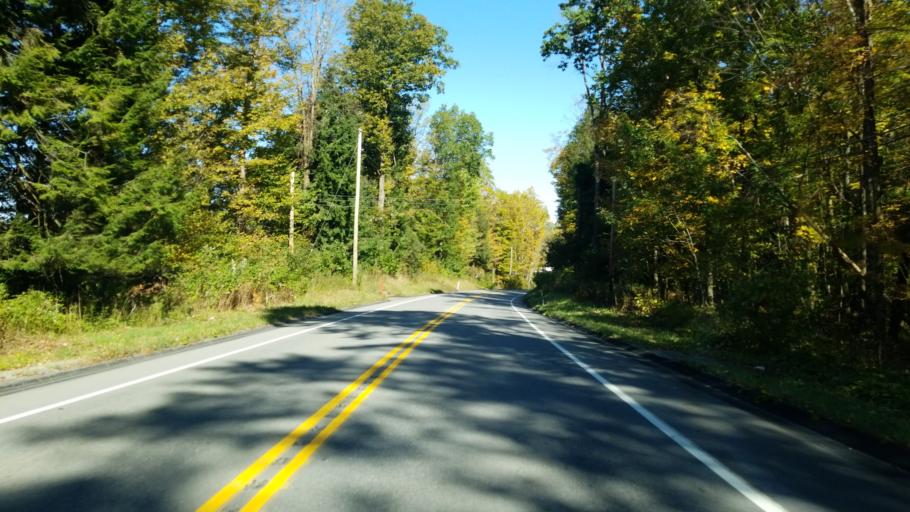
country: US
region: Pennsylvania
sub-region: Clearfield County
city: Treasure Lake
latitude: 41.1822
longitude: -78.6409
